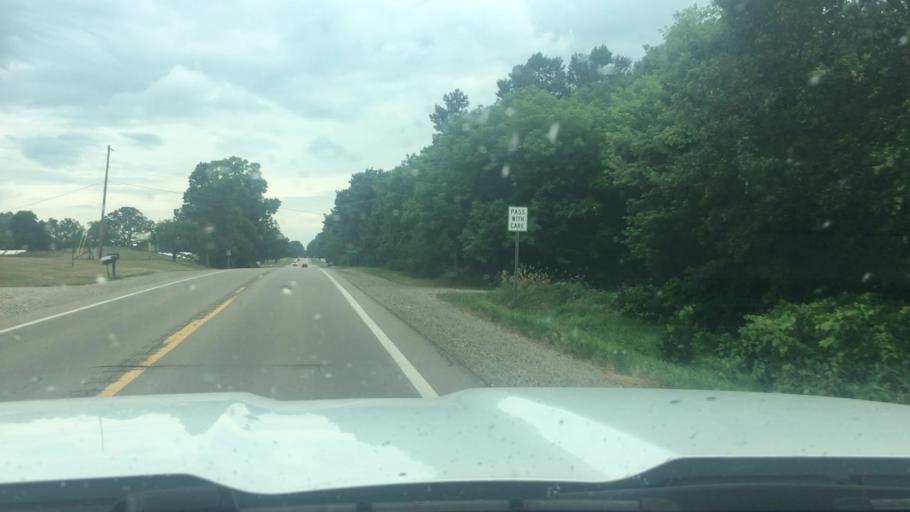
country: US
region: Michigan
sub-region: Ionia County
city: Ionia
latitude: 43.0019
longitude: -84.9910
